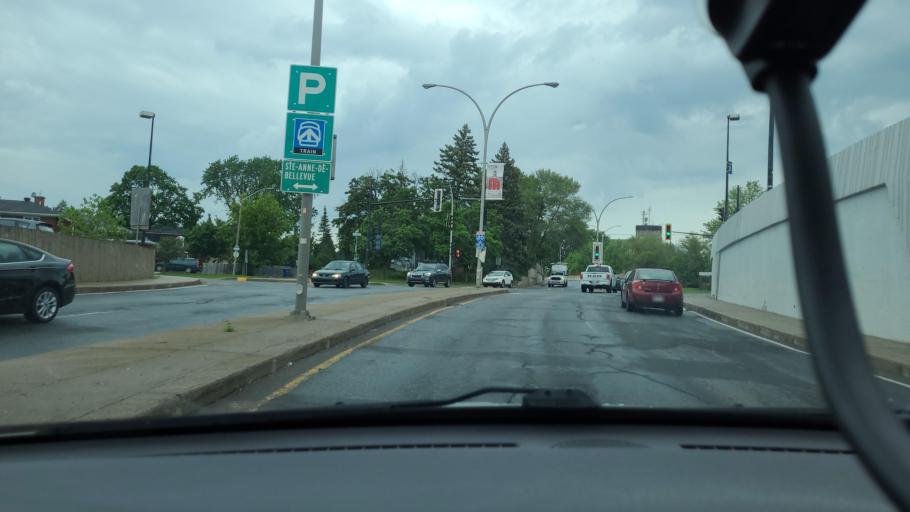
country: CA
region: Quebec
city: Sainte-Anne-de-Bellevue
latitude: 45.4078
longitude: -73.9512
